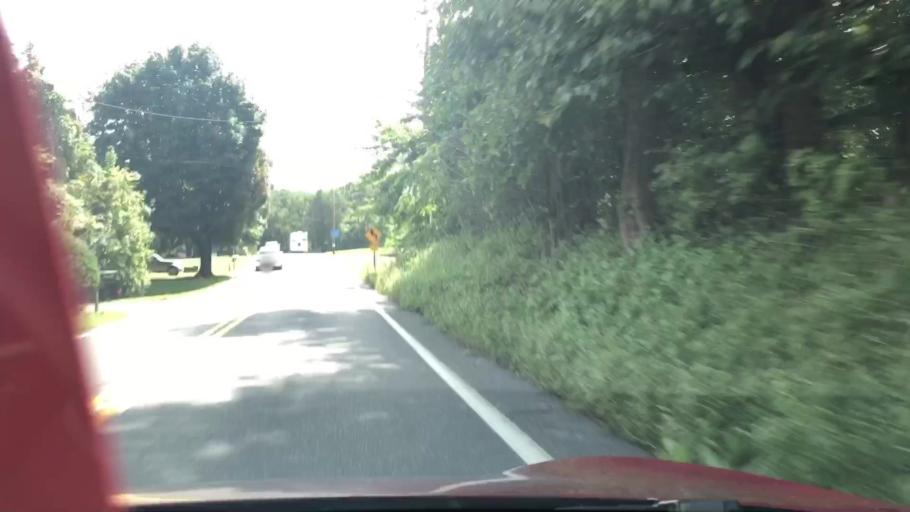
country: US
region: Pennsylvania
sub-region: Dauphin County
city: Skyline View
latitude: 40.3496
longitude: -76.6733
